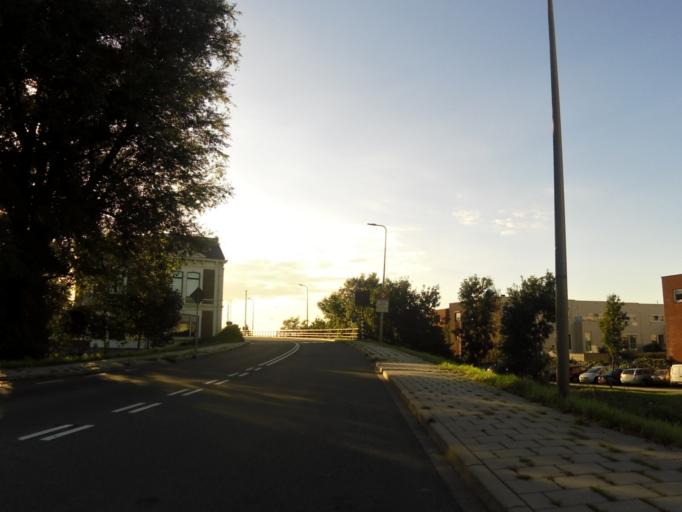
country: NL
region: South Holland
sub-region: Gemeente Alphen aan den Rijn
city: Alphen aan den Rijn
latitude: 52.1429
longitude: 4.6492
